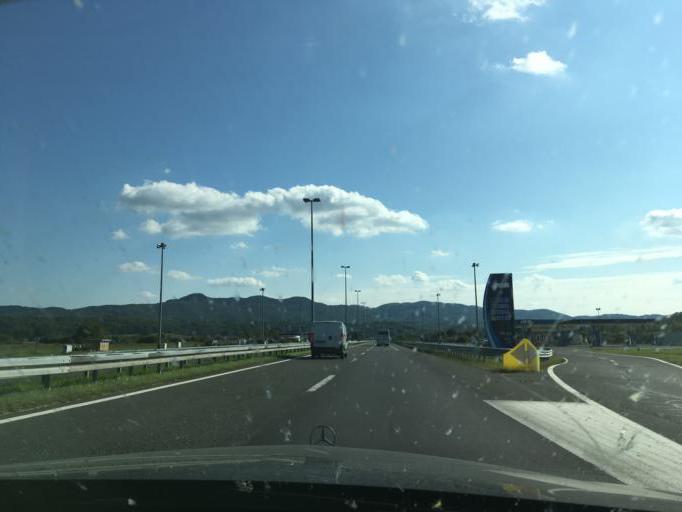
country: HR
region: Varazdinska
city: Ljubescica
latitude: 46.1719
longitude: 16.3754
